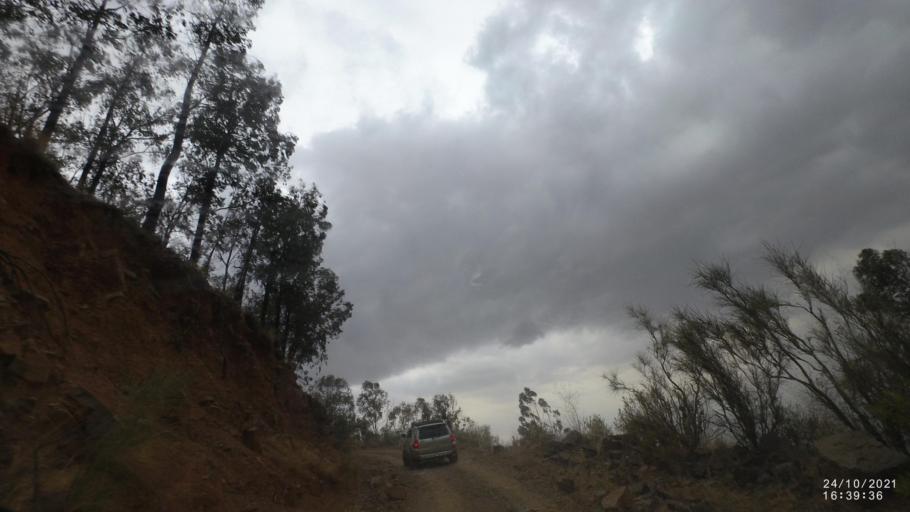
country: BO
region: Cochabamba
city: Cochabamba
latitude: -17.3401
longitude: -66.1491
